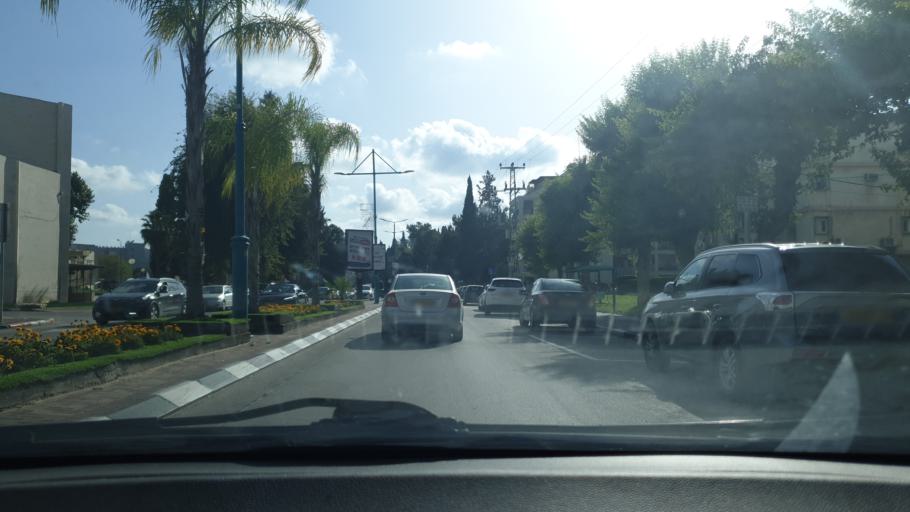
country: IL
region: Central District
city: Ramla
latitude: 31.9294
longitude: 34.8655
